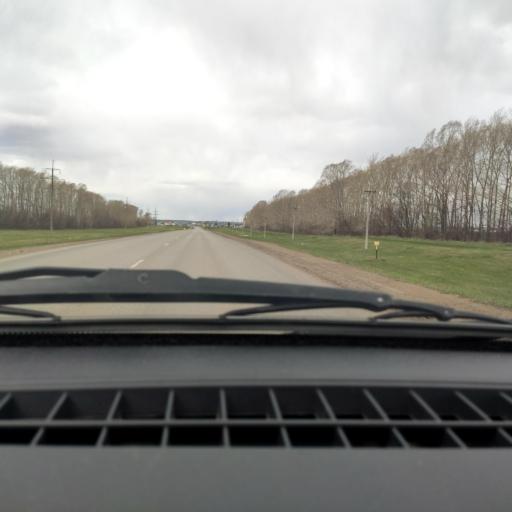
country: RU
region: Bashkortostan
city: Kushnarenkovo
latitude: 55.0744
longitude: 55.4055
